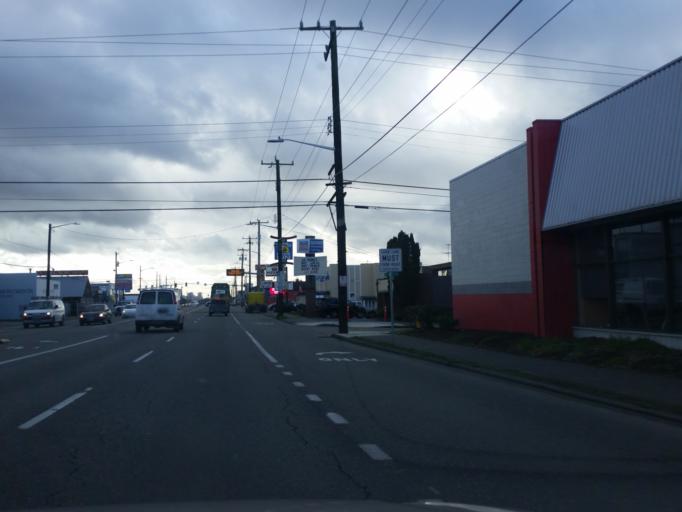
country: US
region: Washington
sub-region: King County
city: Shoreline
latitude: 47.7000
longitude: -122.3447
